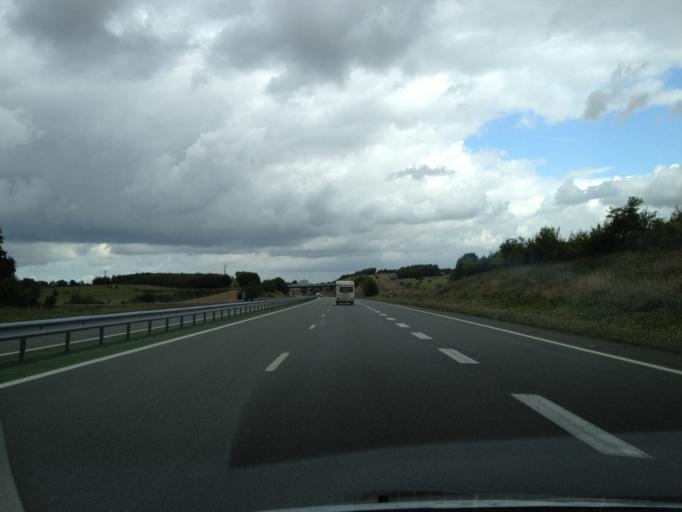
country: FR
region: Pays de la Loire
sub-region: Departement de Maine-et-Loire
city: Nuaille
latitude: 47.0867
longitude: -0.8240
